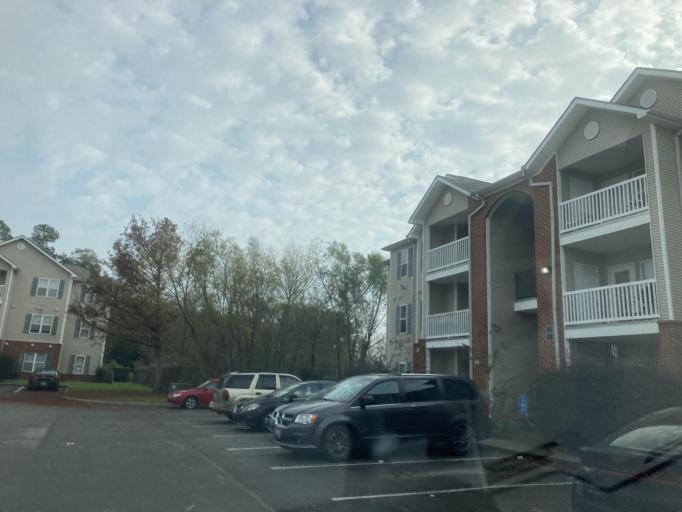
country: US
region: Mississippi
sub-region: Harrison County
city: Gulfport
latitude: 30.3689
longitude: -89.1203
